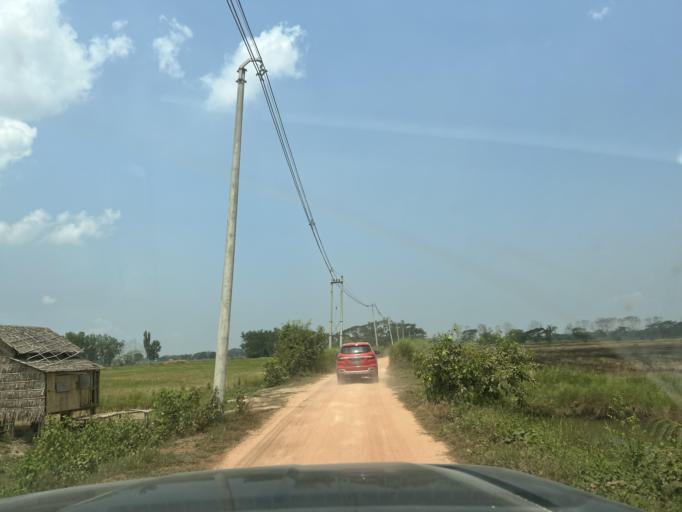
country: MM
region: Yangon
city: Kanbe
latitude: 16.7811
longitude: 96.0212
